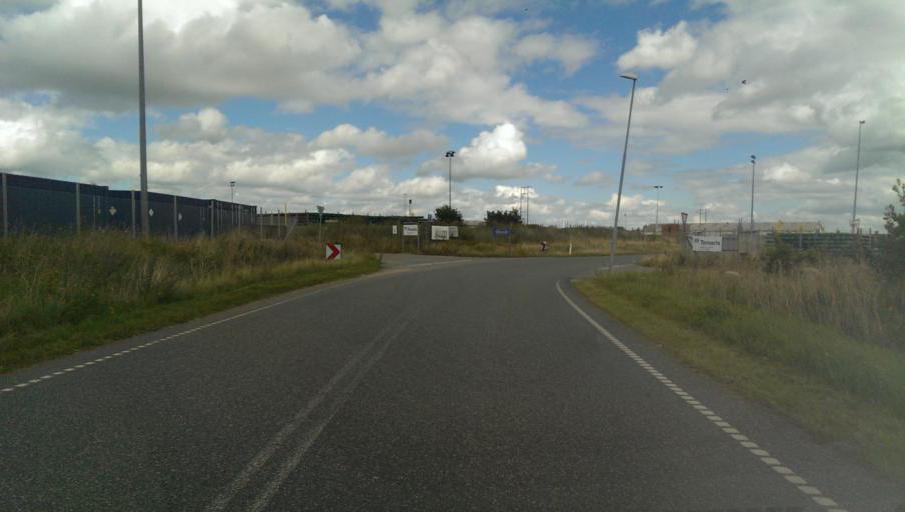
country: DK
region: South Denmark
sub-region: Esbjerg Kommune
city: Esbjerg
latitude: 55.4638
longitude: 8.5086
